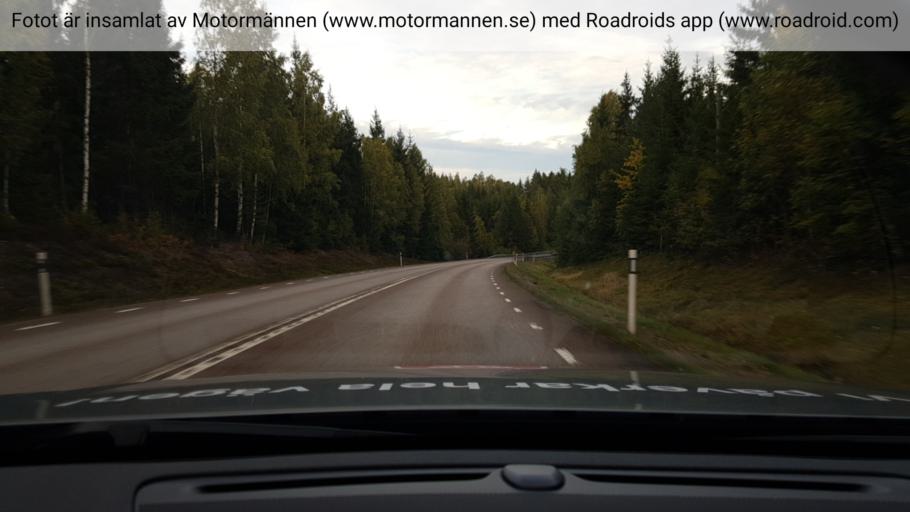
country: SE
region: Vaestra Goetaland
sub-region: Amals Kommun
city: Amal
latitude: 59.0596
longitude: 12.5092
